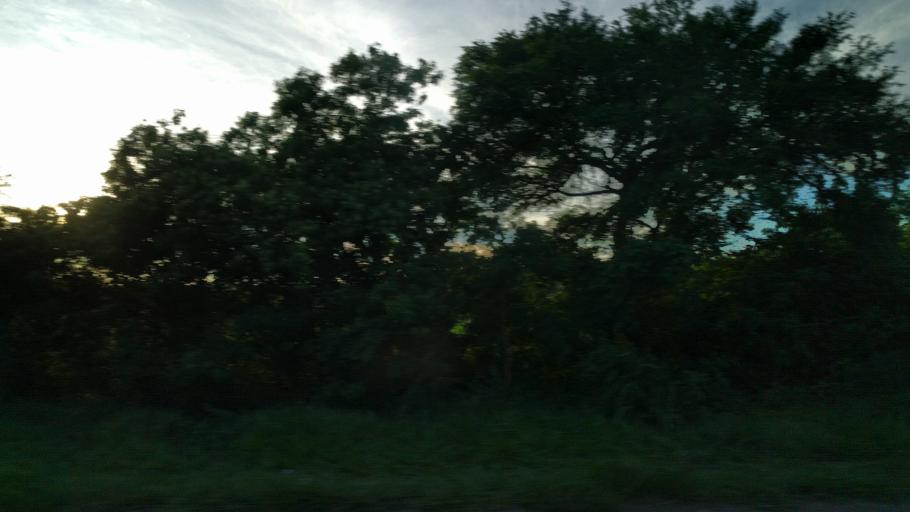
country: BO
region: Santa Cruz
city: Abapo
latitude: -18.5259
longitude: -63.2184
